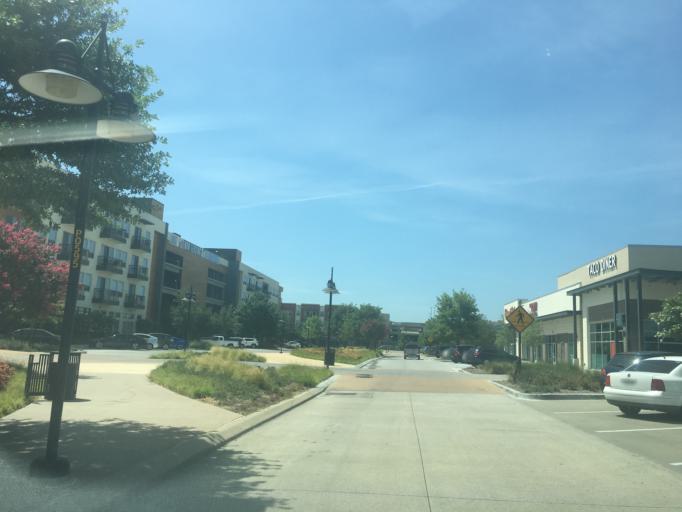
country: US
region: Texas
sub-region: Dallas County
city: Richardson
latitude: 32.8776
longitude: -96.7333
